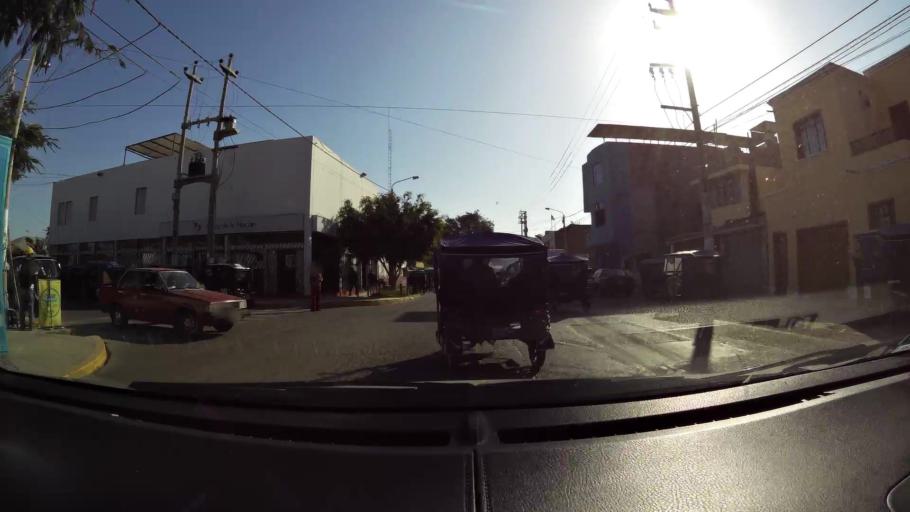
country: PE
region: Ancash
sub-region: Provincia de Casma
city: Casma
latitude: -9.4756
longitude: -78.3044
